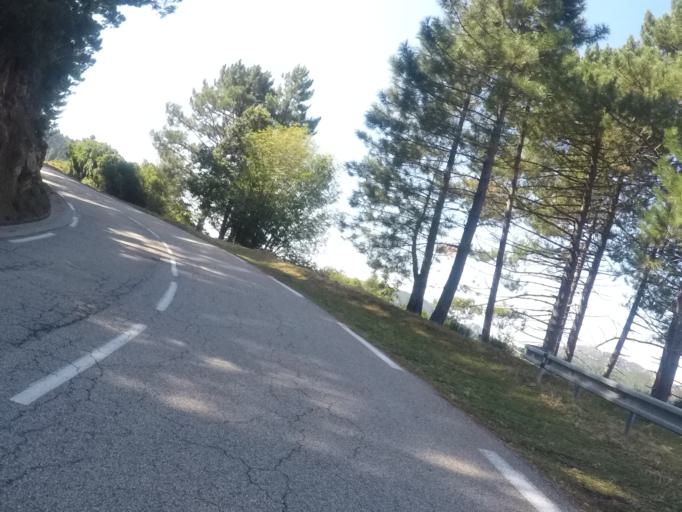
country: FR
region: Corsica
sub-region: Departement de la Corse-du-Sud
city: Zonza
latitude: 41.7737
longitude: 9.0748
